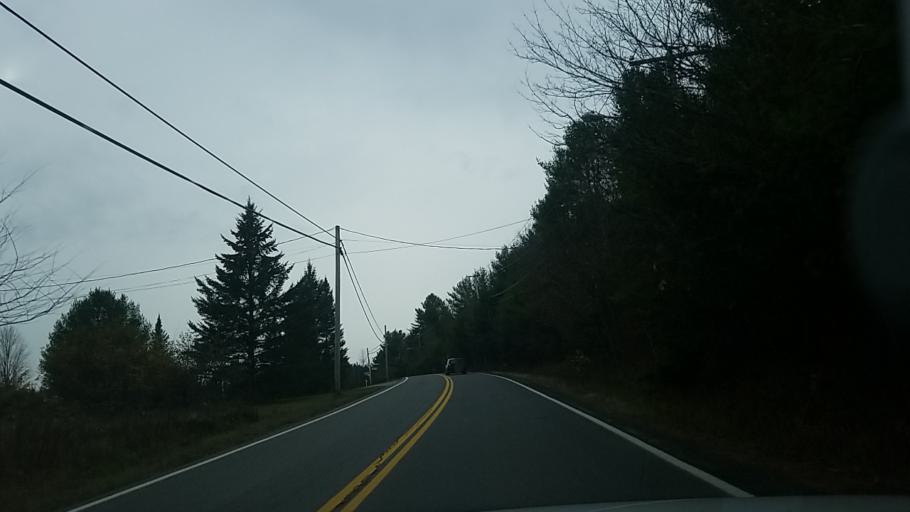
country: CA
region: Quebec
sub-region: Laurentides
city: Saint-Colomban
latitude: 45.7841
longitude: -74.0961
